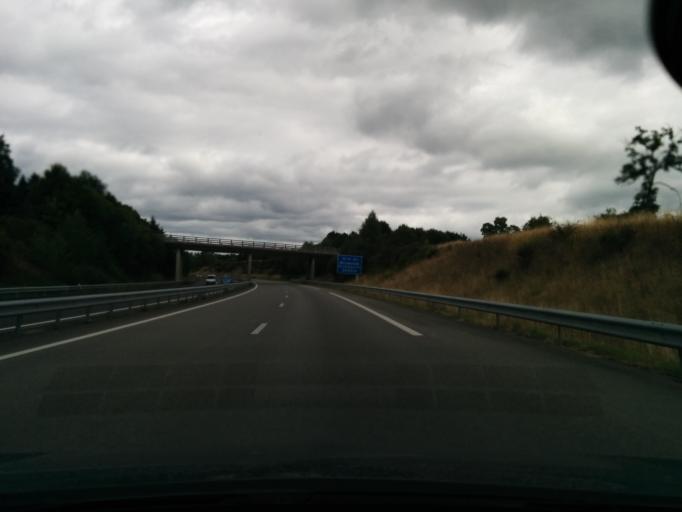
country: FR
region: Limousin
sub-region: Departement de la Haute-Vienne
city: Arnac-la-Poste
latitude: 46.2908
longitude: 1.4158
